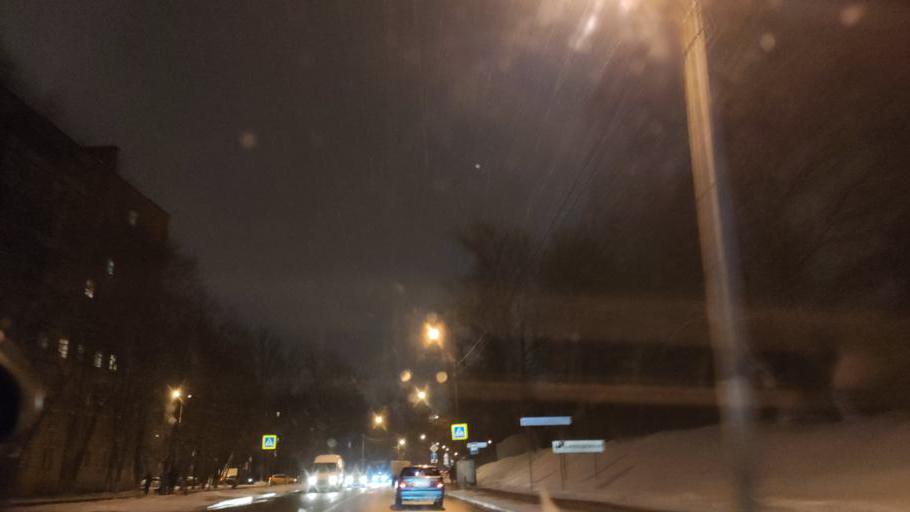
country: RU
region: Moskovskaya
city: Odintsovo
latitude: 55.6741
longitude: 37.2524
